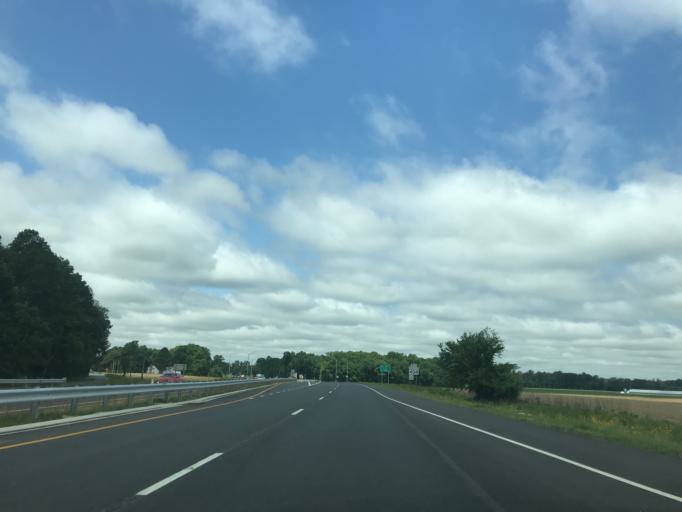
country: US
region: Maryland
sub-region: Caroline County
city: Ridgely
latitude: 38.9160
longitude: -75.8958
